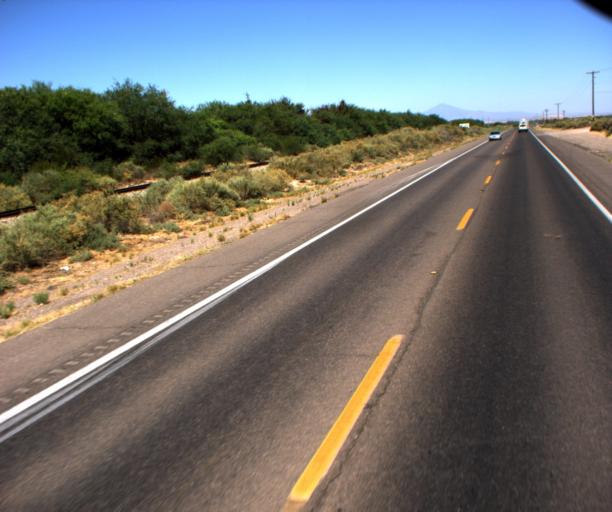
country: US
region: Arizona
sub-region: Graham County
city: Pima
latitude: 32.9266
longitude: -109.8809
